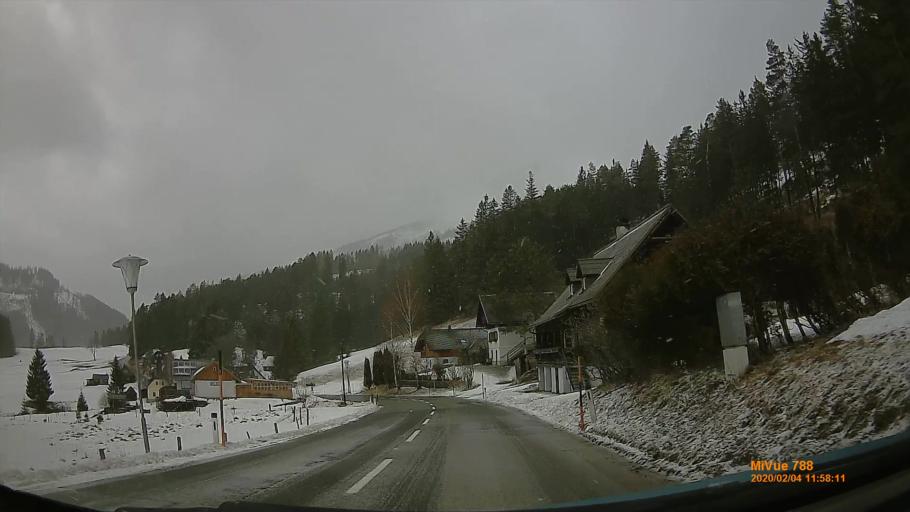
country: AT
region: Styria
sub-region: Politischer Bezirk Bruck-Muerzzuschlag
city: Muerzsteg
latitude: 47.7726
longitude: 15.5066
